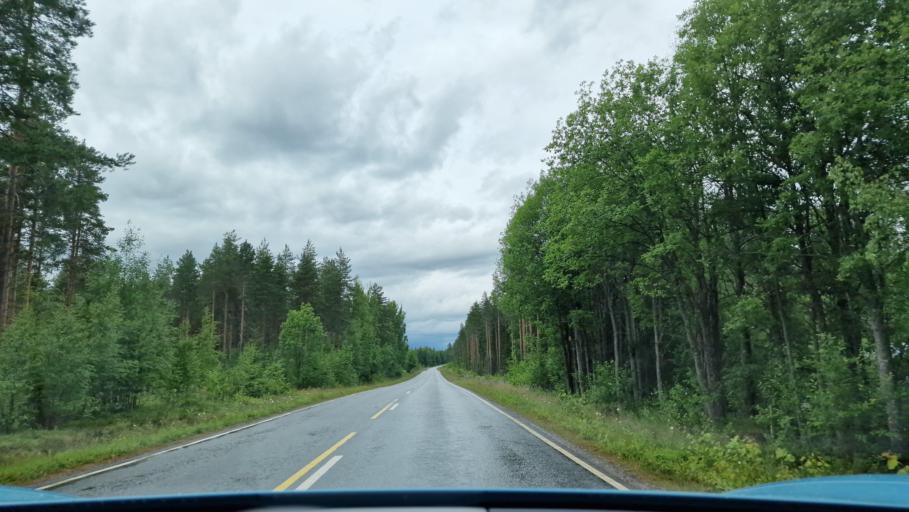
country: FI
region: Central Finland
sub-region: Saarijaervi-Viitasaari
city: Pylkoenmaeki
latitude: 62.6739
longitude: 24.5089
